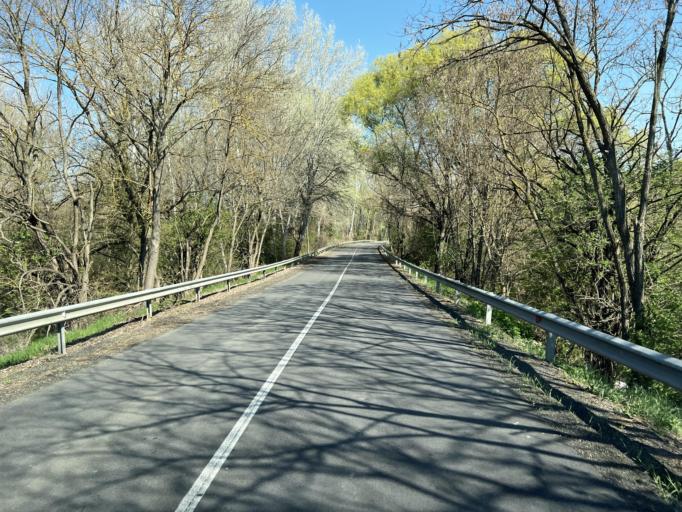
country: HU
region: Pest
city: Orbottyan
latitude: 47.7294
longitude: 19.2693
